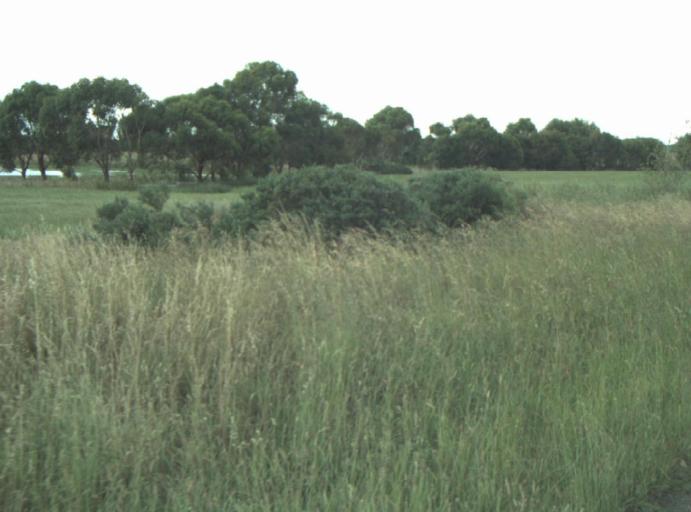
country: AU
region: Victoria
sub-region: Greater Geelong
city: Clifton Springs
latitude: -38.1901
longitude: 144.5886
